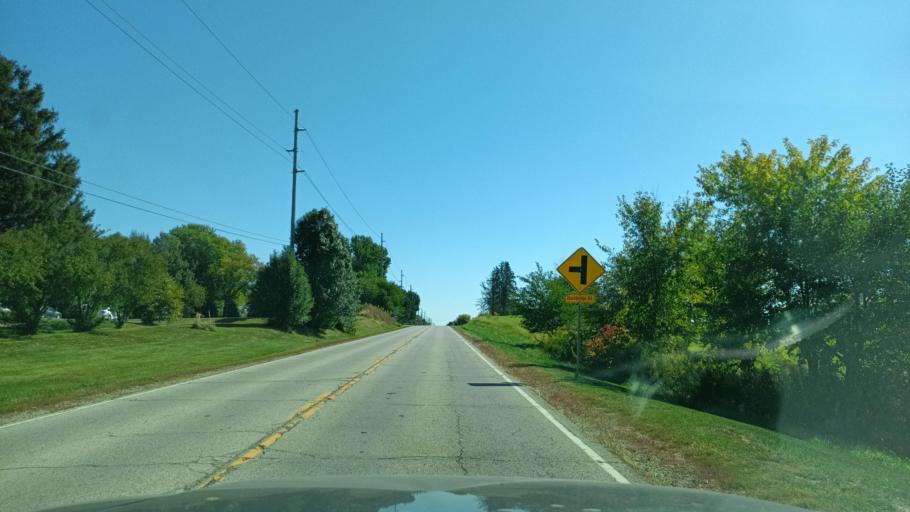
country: US
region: Illinois
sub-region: Peoria County
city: Dunlap
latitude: 40.7843
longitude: -89.7173
